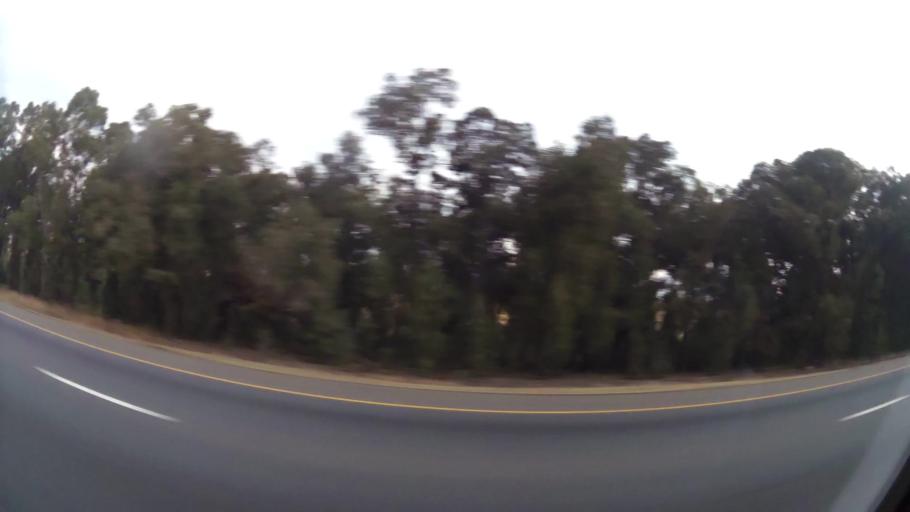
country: ZA
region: Gauteng
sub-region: Ekurhuleni Metropolitan Municipality
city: Germiston
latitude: -26.2516
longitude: 28.2221
